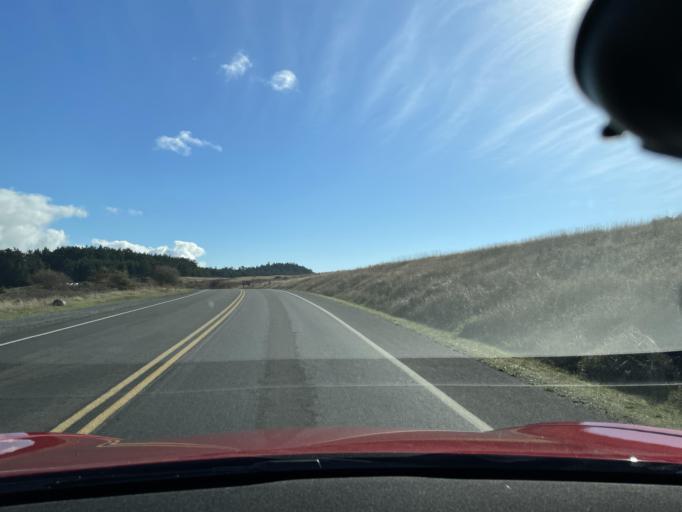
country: US
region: Washington
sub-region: San Juan County
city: Friday Harbor
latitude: 48.4645
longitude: -123.0042
